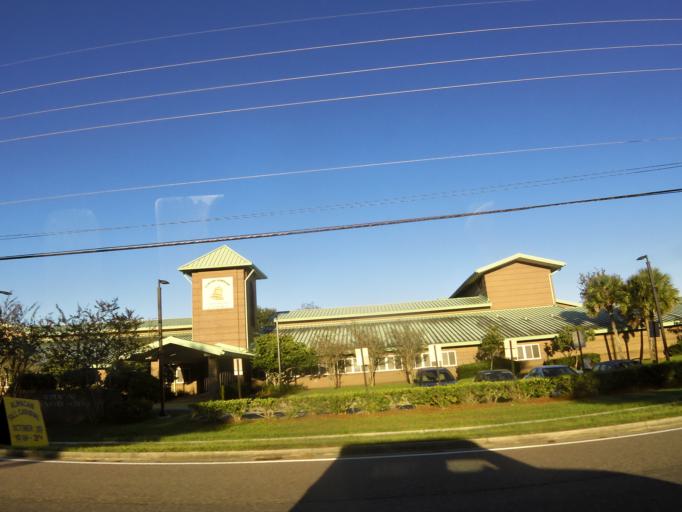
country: US
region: Florida
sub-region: Duval County
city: Neptune Beach
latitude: 30.3140
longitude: -81.4479
